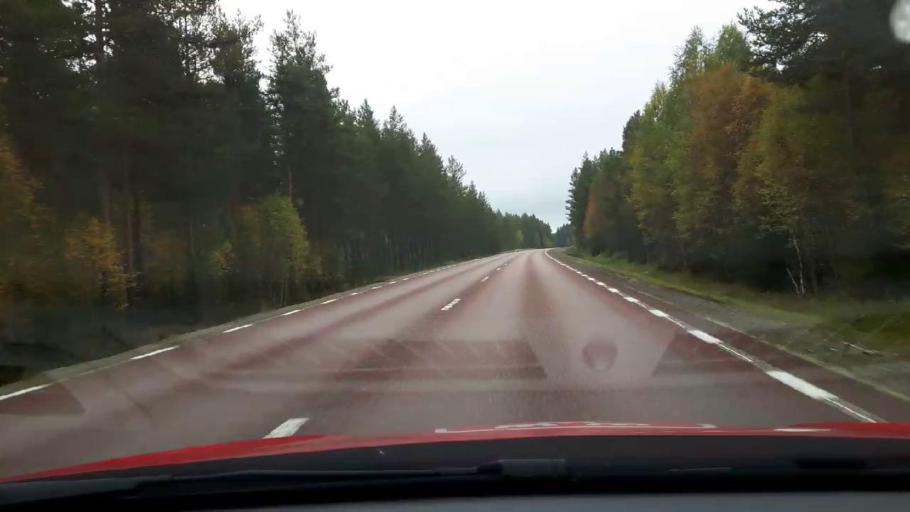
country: SE
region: Gaevleborg
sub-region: Ljusdals Kommun
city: Farila
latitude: 61.8266
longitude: 15.7543
